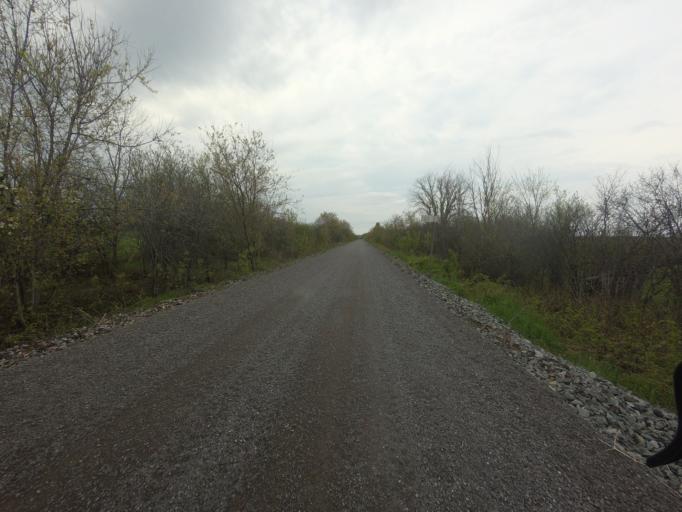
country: CA
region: Ontario
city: Carleton Place
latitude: 45.2147
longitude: -76.1810
